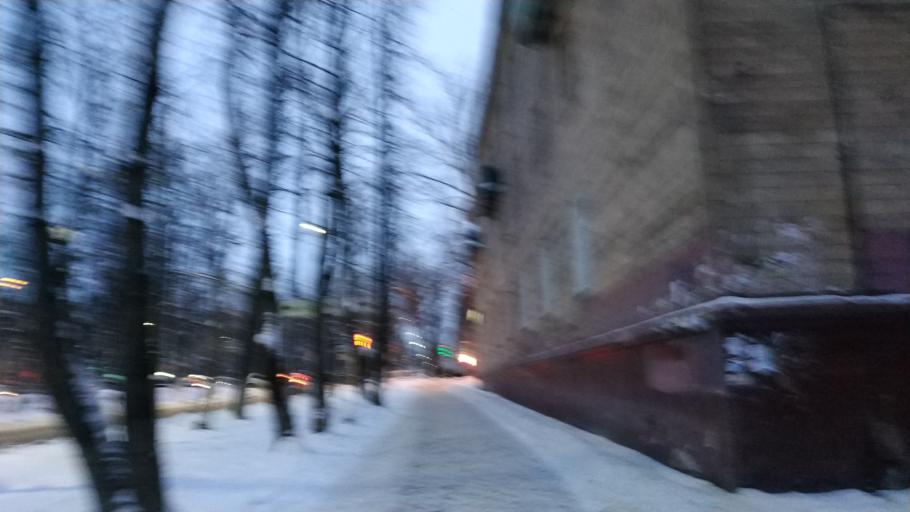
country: RU
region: Moskovskaya
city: Shchelkovo
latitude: 55.9217
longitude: 37.9762
